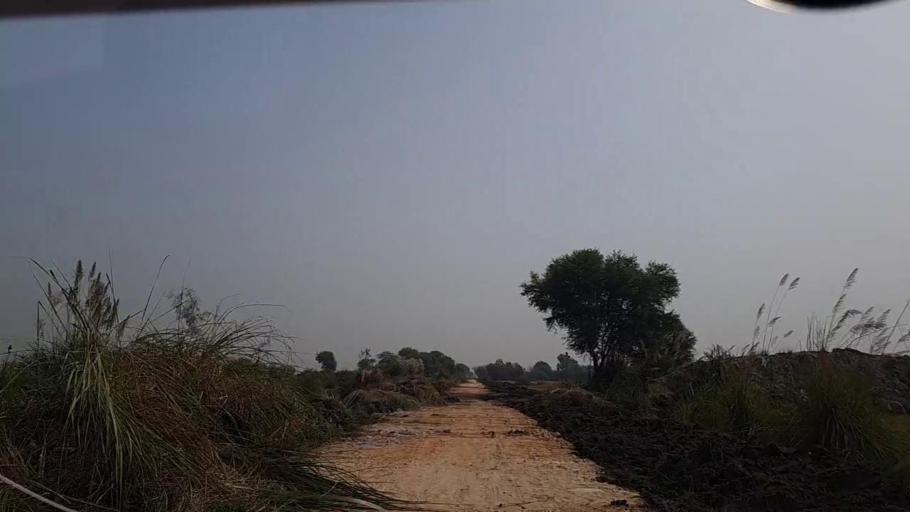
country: PK
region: Sindh
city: Shikarpur
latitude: 27.9204
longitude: 68.5796
